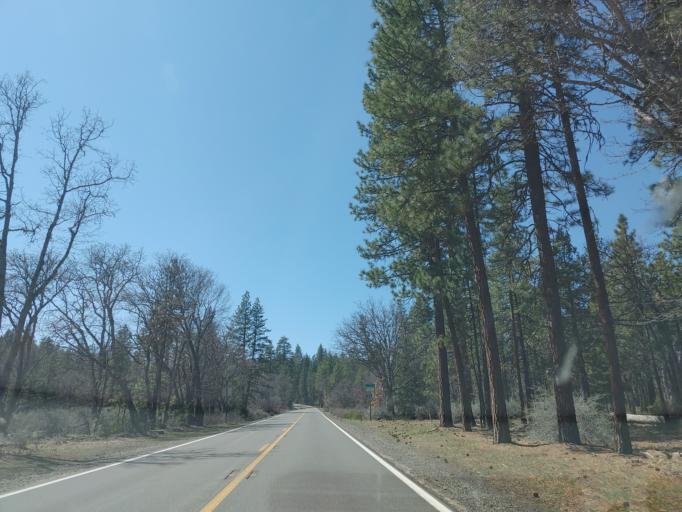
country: US
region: California
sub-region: Shasta County
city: Burney
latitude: 41.0158
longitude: -121.6426
